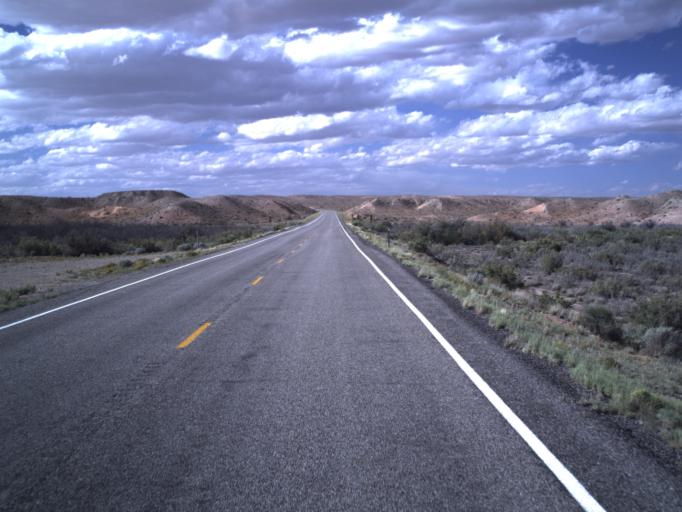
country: US
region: Utah
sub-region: Emery County
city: Ferron
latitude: 38.3239
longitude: -110.6762
